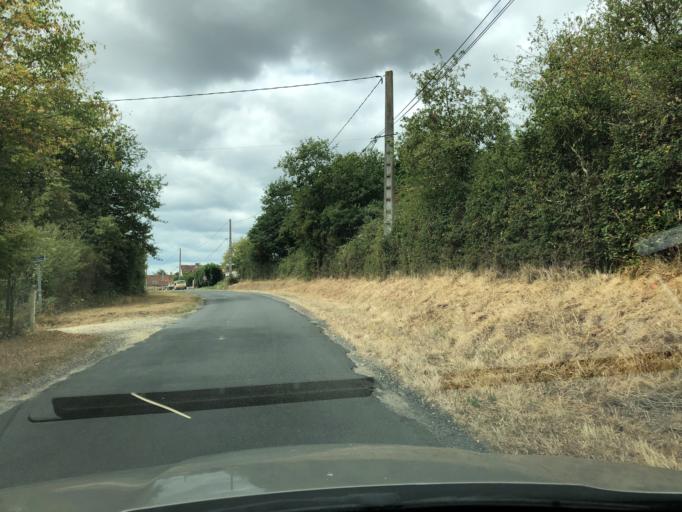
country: FR
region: Centre
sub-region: Departement d'Indre-et-Loire
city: Mazieres-de-Touraine
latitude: 47.3901
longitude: 0.4565
